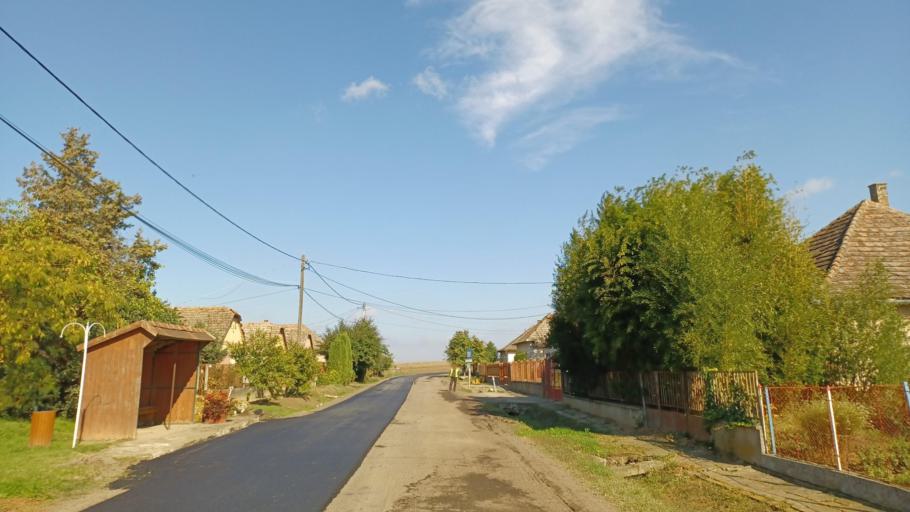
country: HU
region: Tolna
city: Nagydorog
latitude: 46.6062
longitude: 18.5942
